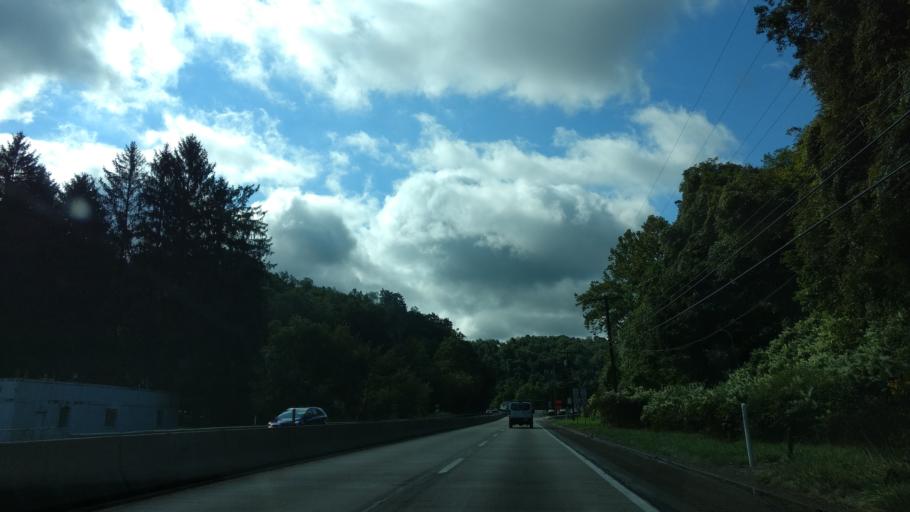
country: US
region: Pennsylvania
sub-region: Allegheny County
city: Elizabeth
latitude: 40.2527
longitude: -79.8785
